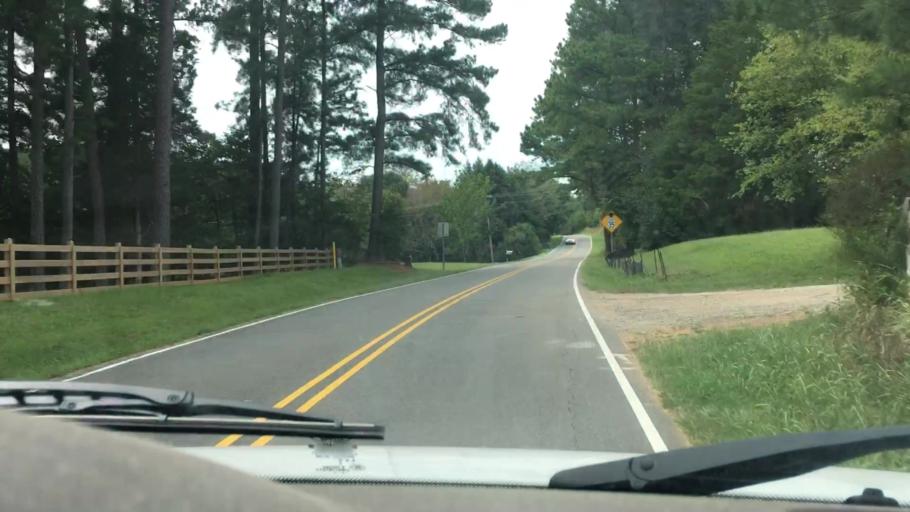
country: US
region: North Carolina
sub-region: Gaston County
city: Davidson
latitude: 35.4987
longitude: -80.8214
